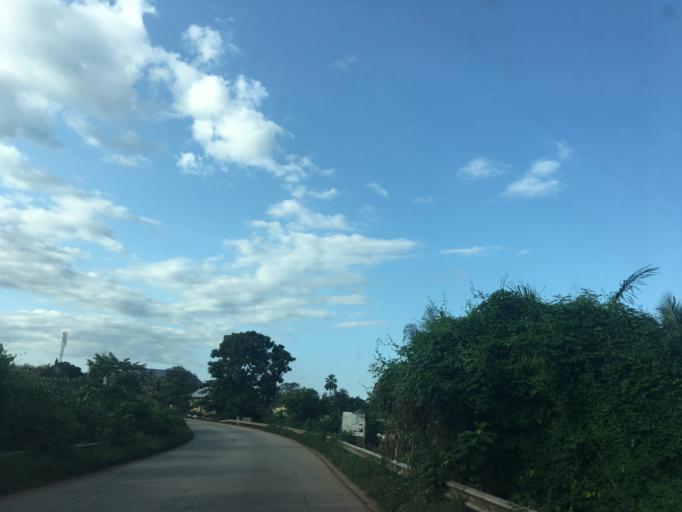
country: GH
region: Western
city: Bibiani
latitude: 6.3269
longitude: -2.2503
